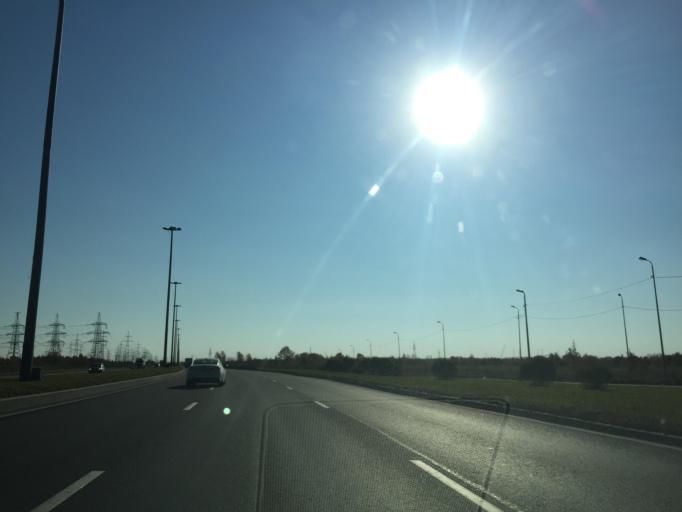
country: RU
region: St.-Petersburg
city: Petro-Slavyanka
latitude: 59.7659
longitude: 30.5029
